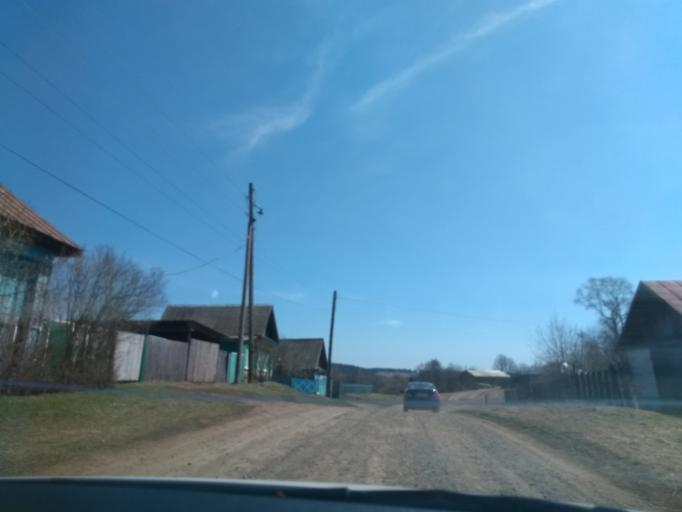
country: RU
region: Perm
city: Uinskoye
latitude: 57.1776
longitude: 56.5716
